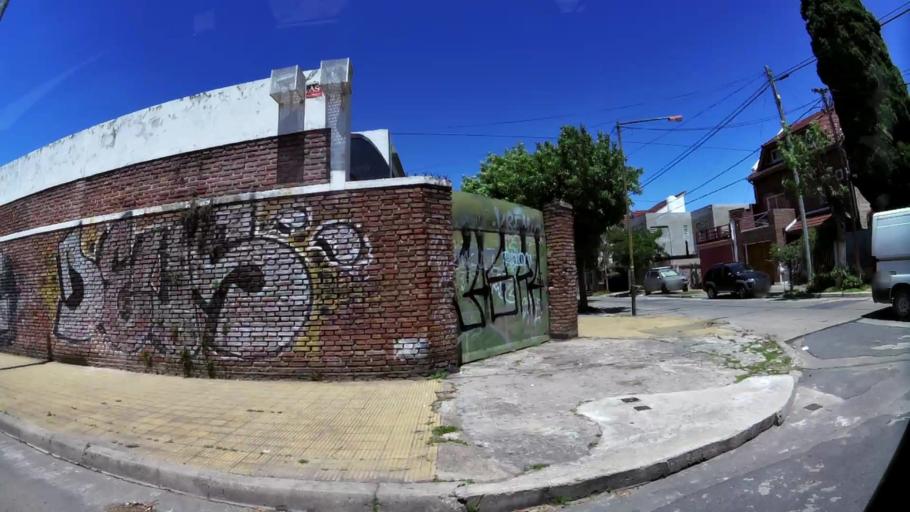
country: AR
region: Buenos Aires
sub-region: Partido de San Isidro
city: San Isidro
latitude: -34.4935
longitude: -58.5148
